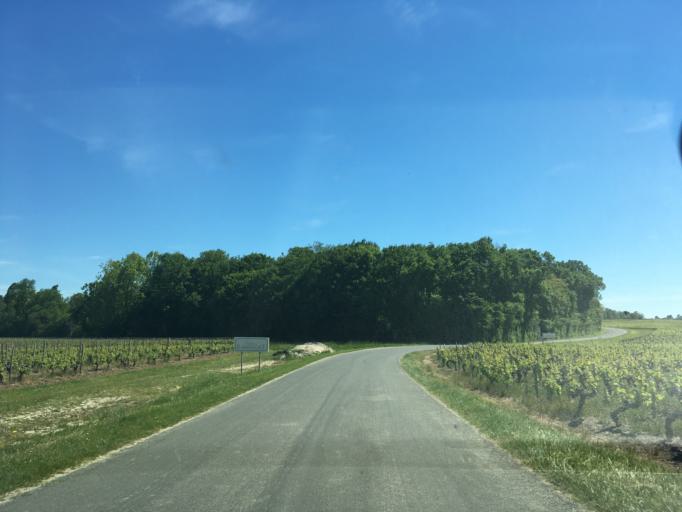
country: FR
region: Aquitaine
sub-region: Departement de la Gironde
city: Lesparre-Medoc
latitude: 45.3177
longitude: -0.8812
